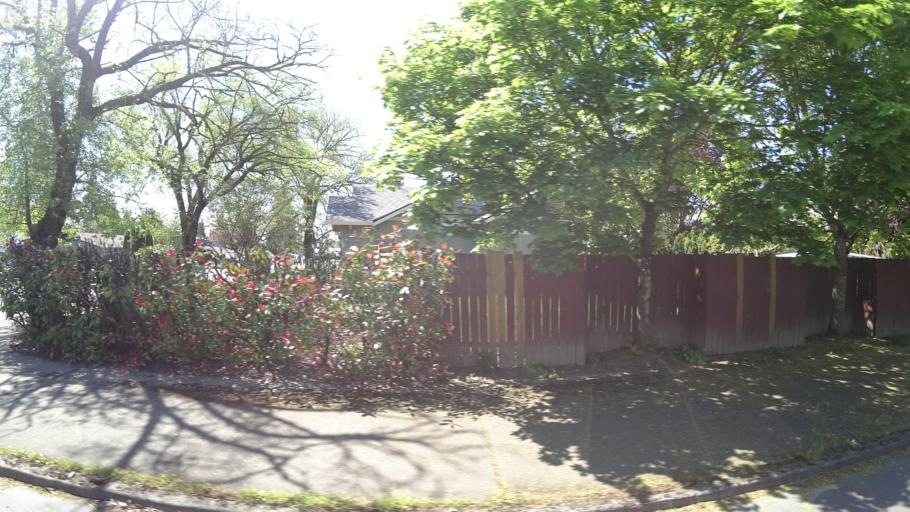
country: US
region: Oregon
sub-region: Washington County
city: Hillsboro
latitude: 45.5069
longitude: -122.9660
